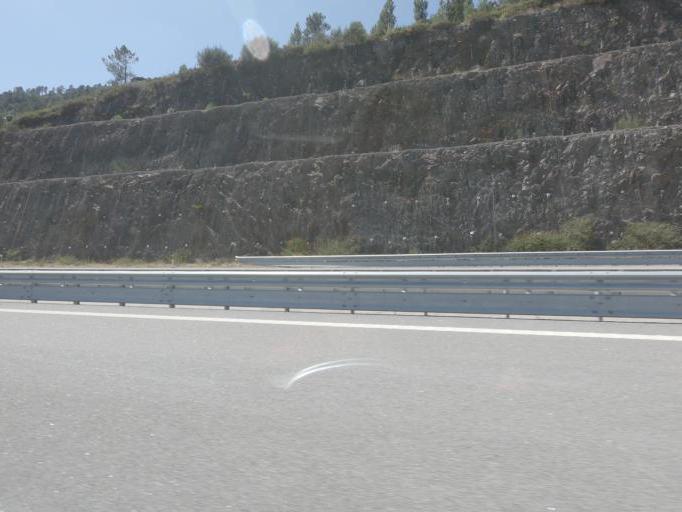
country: PT
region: Vila Real
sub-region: Mesao Frio
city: Mesao Frio
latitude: 41.2638
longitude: -7.9425
